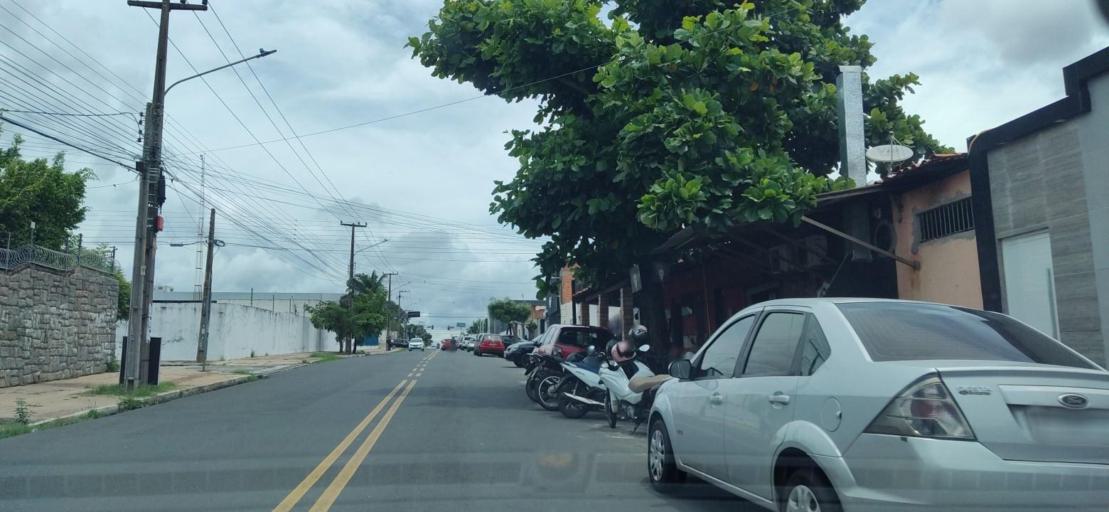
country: BR
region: Piaui
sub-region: Teresina
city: Teresina
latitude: -5.0833
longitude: -42.8012
